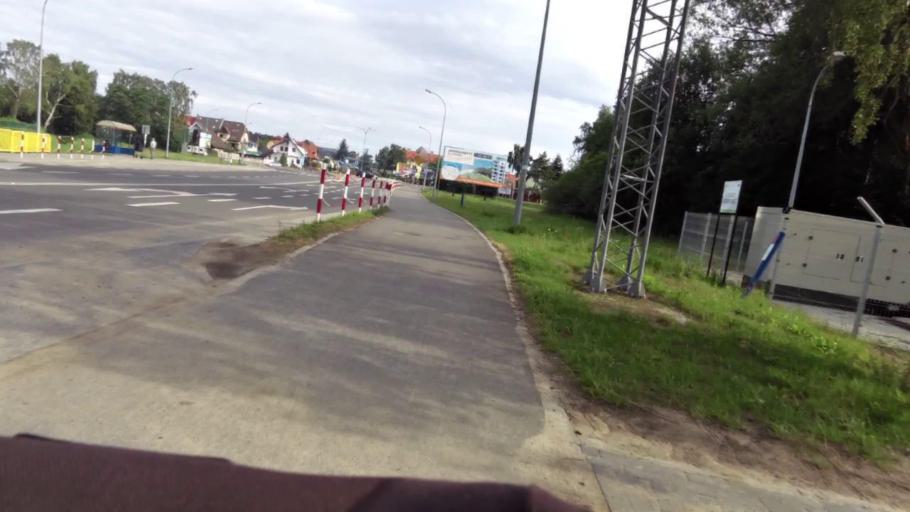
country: PL
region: West Pomeranian Voivodeship
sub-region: Powiat kamienski
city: Dziwnow
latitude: 54.0315
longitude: 14.8079
